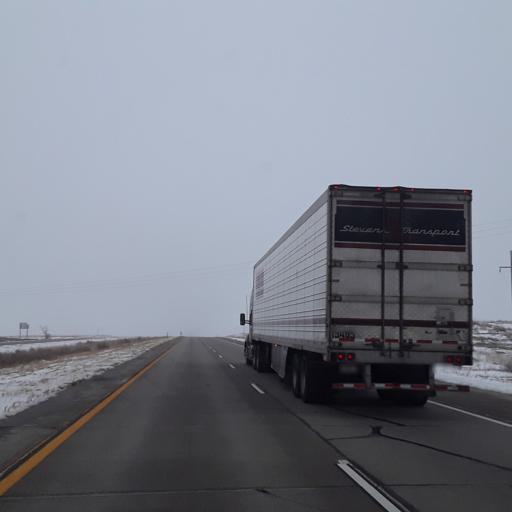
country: US
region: Colorado
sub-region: Logan County
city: Sterling
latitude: 40.7185
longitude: -103.0381
